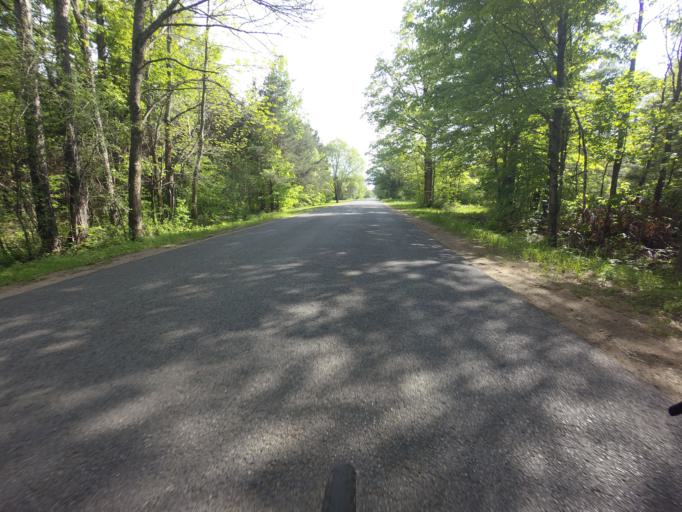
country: US
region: New York
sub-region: St. Lawrence County
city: Gouverneur
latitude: 44.2295
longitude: -75.2277
